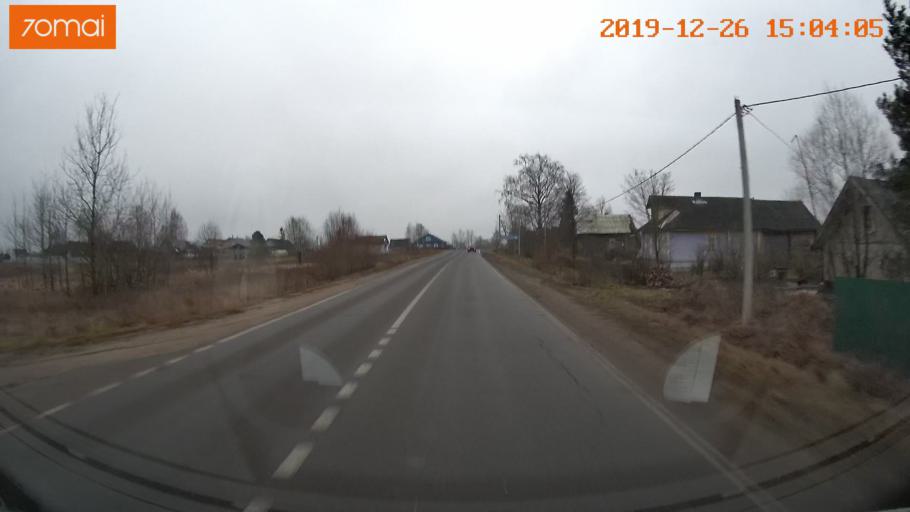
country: RU
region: Jaroslavl
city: Rybinsk
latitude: 58.2041
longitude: 38.8656
